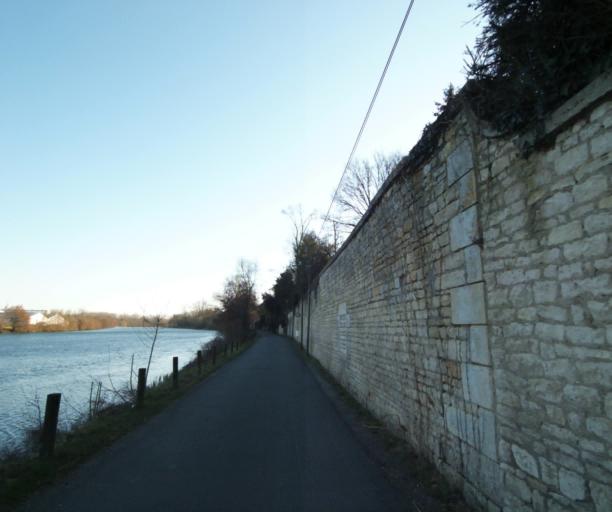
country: FR
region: Poitou-Charentes
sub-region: Departement des Deux-Sevres
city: Niort
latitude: 46.3337
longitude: -0.4939
